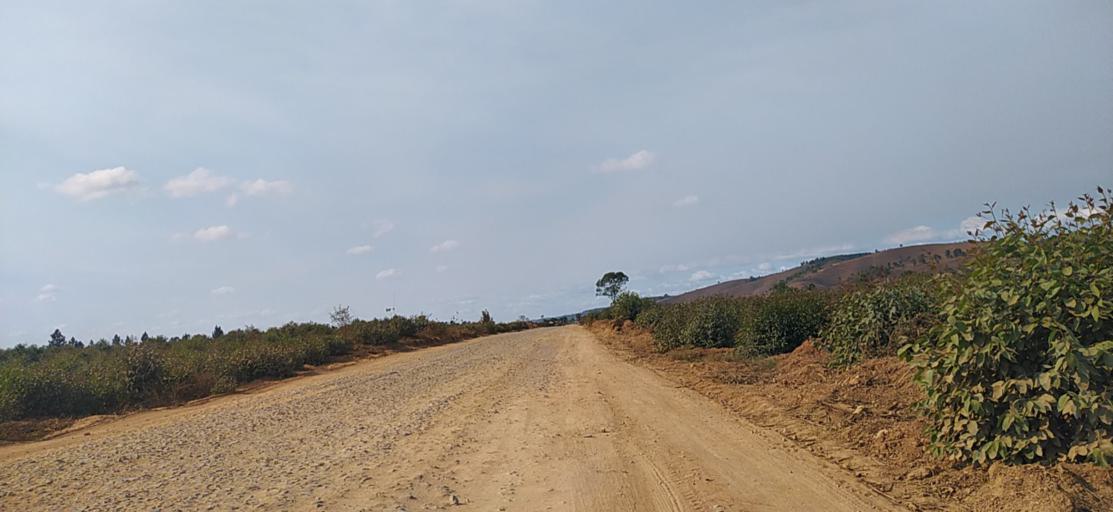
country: MG
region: Alaotra Mangoro
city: Moramanga
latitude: -18.6794
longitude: 48.2724
